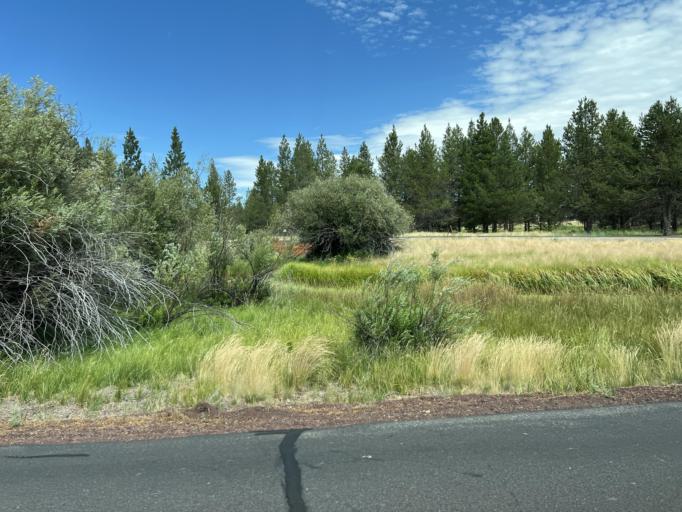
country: US
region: Oregon
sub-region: Deschutes County
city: Sunriver
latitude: 43.8834
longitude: -121.4470
